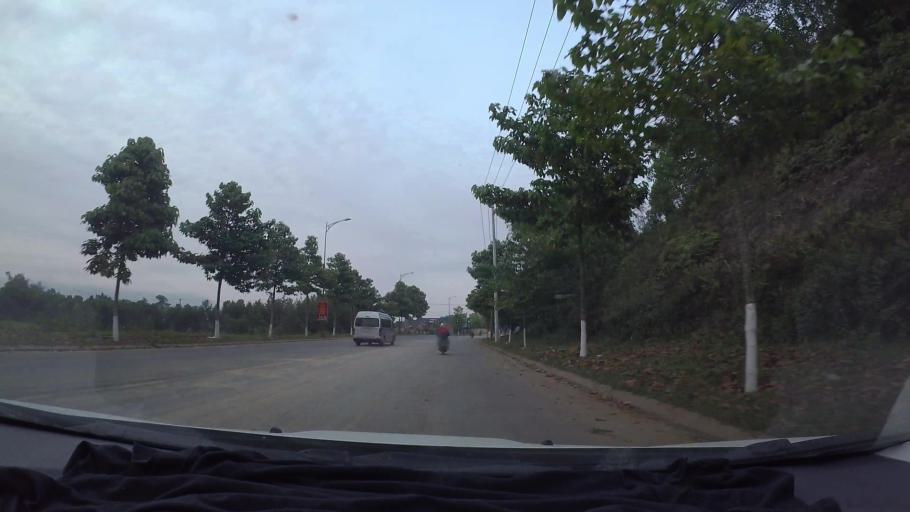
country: VN
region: Da Nang
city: Lien Chieu
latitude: 16.0614
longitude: 108.0993
